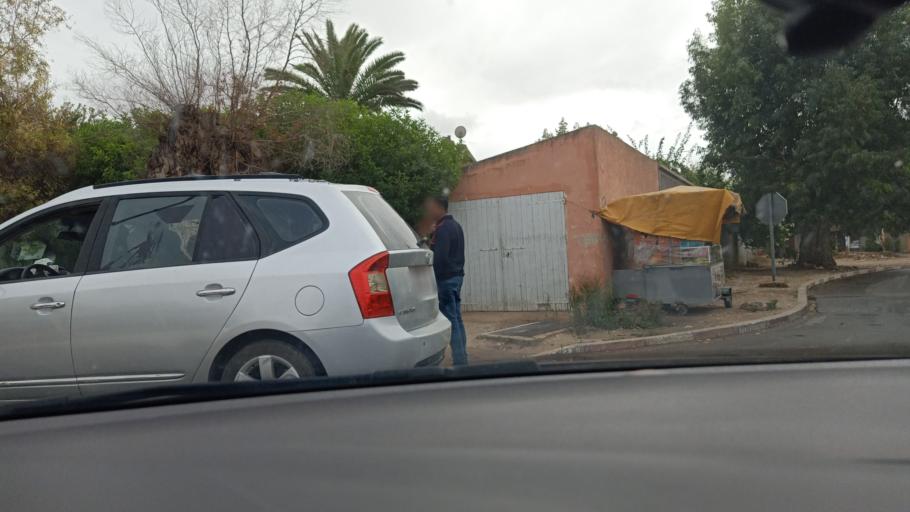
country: MA
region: Doukkala-Abda
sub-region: Safi
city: Youssoufia
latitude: 32.2456
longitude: -8.5311
